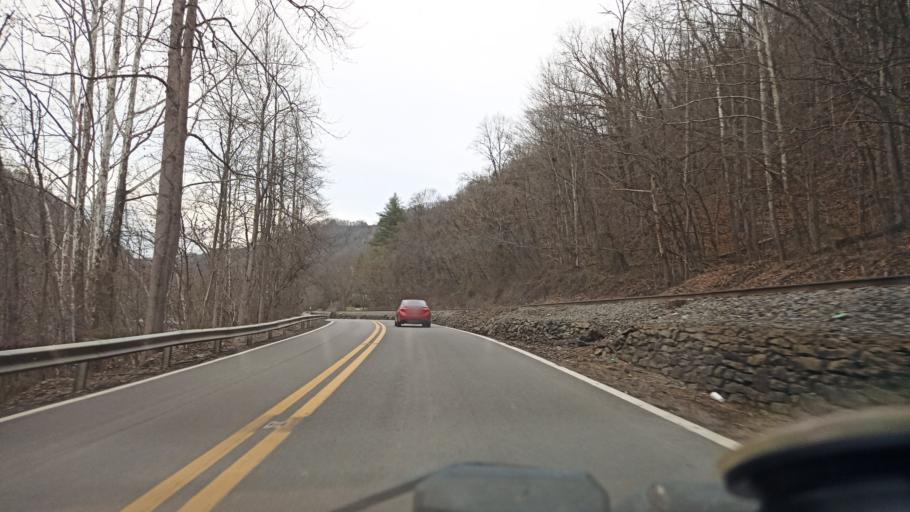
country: US
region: West Virginia
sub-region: Logan County
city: Mallory
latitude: 37.7055
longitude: -81.8665
